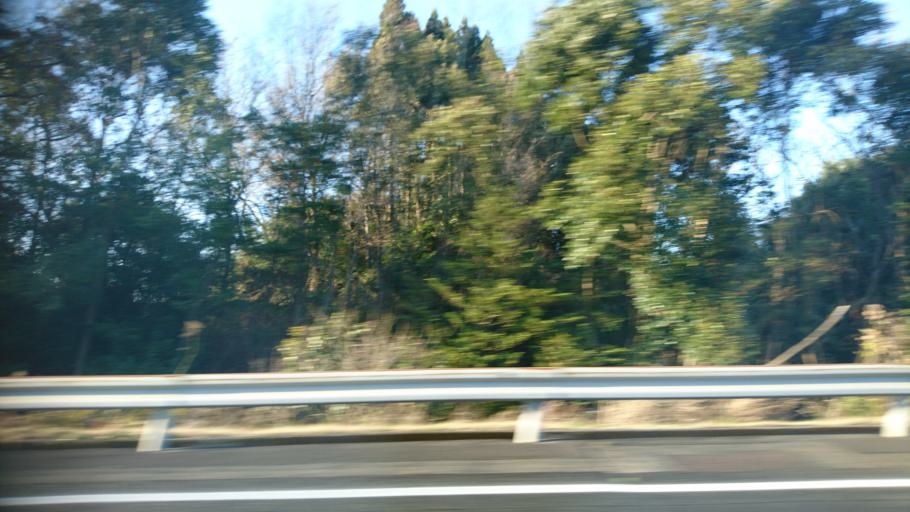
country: JP
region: Miyazaki
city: Miyazaki-shi
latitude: 31.8185
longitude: 131.2732
